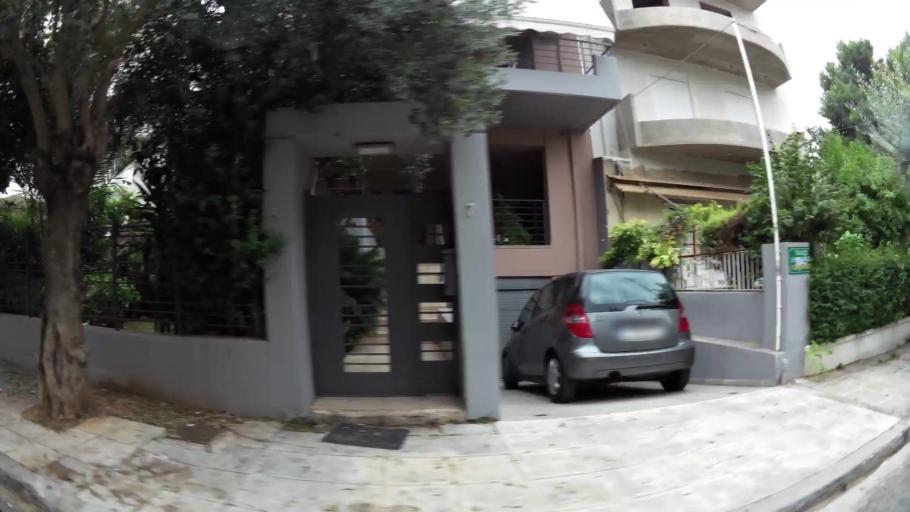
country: GR
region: Attica
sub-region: Nomarchia Athinas
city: Filothei
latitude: 38.0378
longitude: 23.7772
